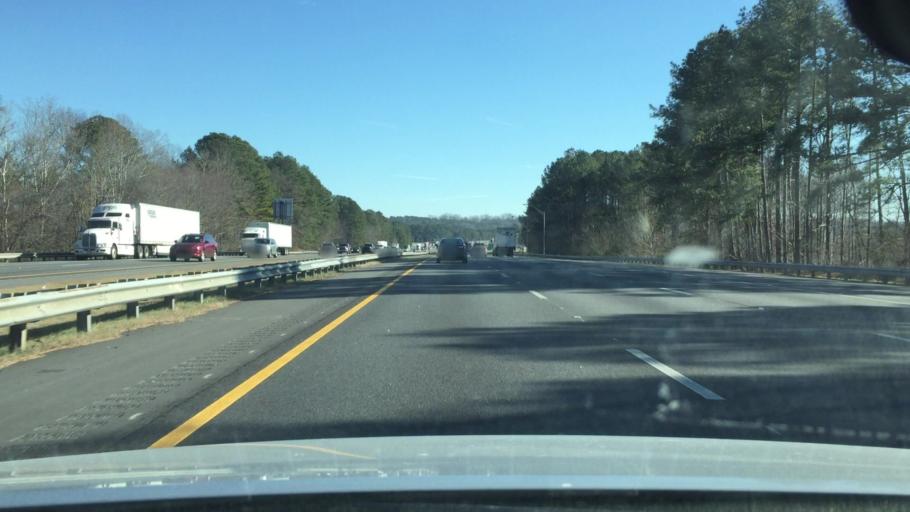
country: US
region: Georgia
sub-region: Catoosa County
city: Ringgold
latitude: 34.8848
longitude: -85.0595
